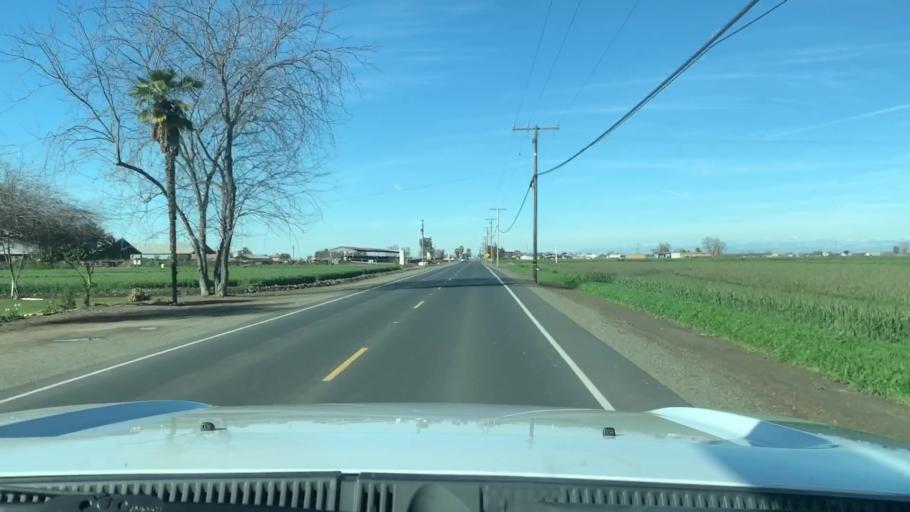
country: US
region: California
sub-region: Kings County
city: Corcoran
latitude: 36.1982
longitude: -119.4931
